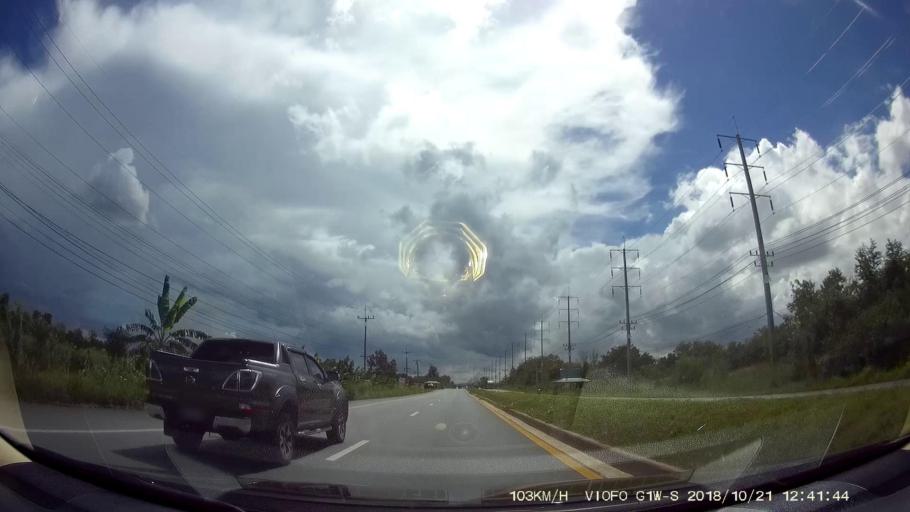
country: TH
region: Nakhon Ratchasima
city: Amphoe Sikhiu
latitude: 15.0085
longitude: 101.6863
